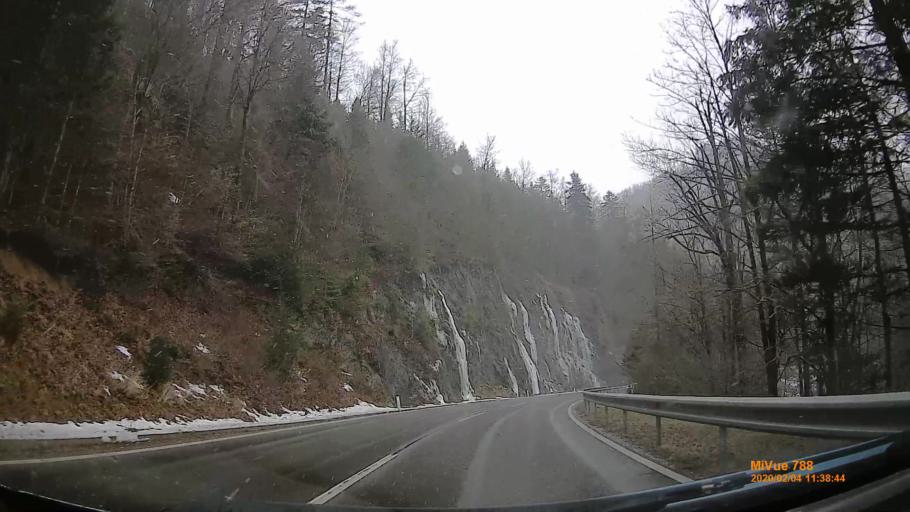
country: AT
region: Styria
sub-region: Politischer Bezirk Bruck-Muerzzuschlag
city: Neuberg an der Muerz
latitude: 47.6626
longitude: 15.5292
